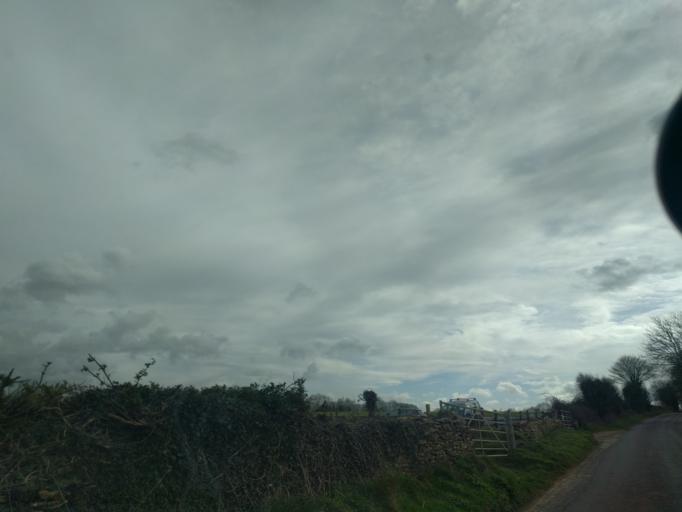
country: GB
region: England
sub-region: Wiltshire
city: Colerne
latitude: 51.4659
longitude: -2.2784
